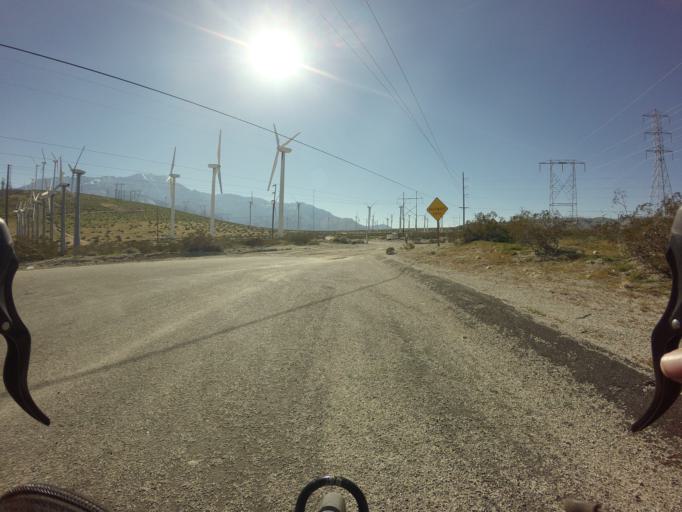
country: US
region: California
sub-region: Riverside County
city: Garnet
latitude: 33.9326
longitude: -116.6144
